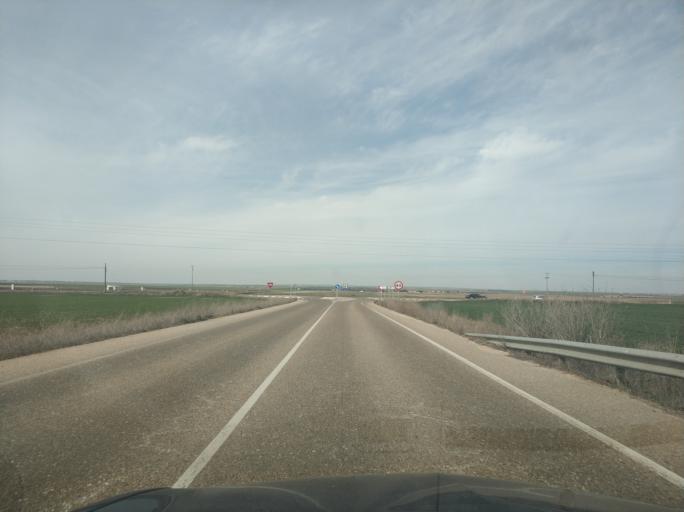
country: ES
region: Castille and Leon
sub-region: Provincia de Salamanca
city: Castellanos de Moriscos
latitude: 41.0312
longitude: -5.5780
